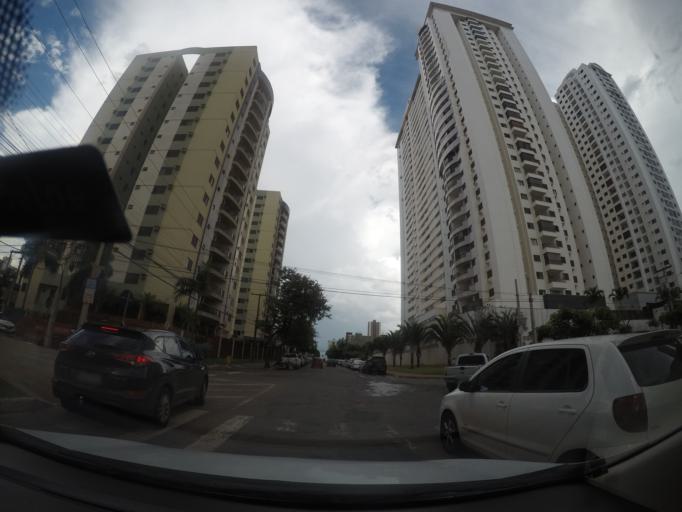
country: BR
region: Goias
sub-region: Goiania
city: Goiania
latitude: -16.7191
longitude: -49.2658
